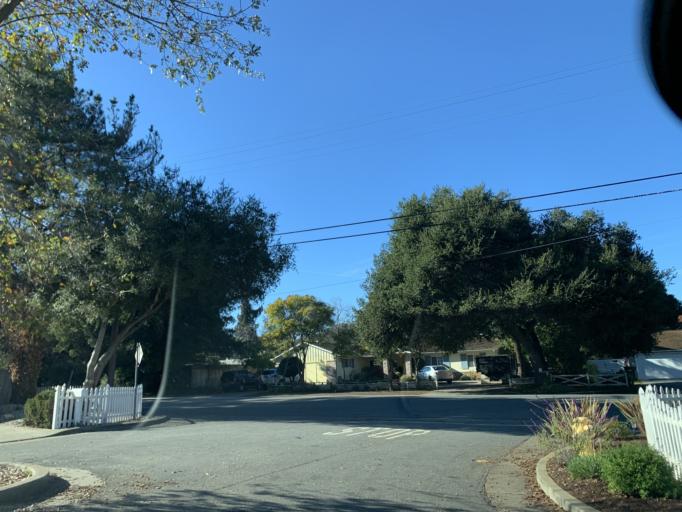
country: US
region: California
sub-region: Santa Clara County
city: Mountain View
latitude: 37.3840
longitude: -122.0978
